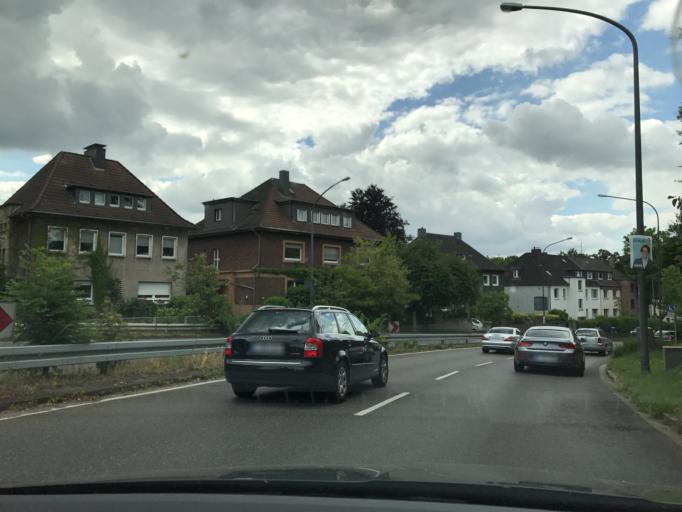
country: DE
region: North Rhine-Westphalia
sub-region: Regierungsbezirk Dusseldorf
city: Essen
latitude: 51.4088
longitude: 6.9933
